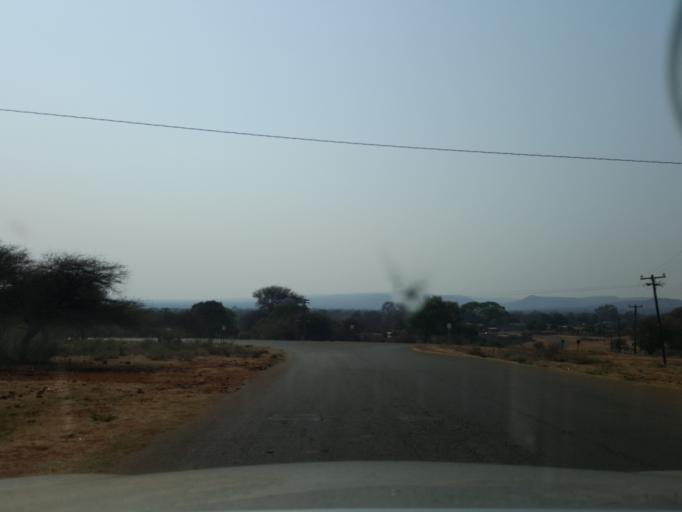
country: BW
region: South East
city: Lobatse
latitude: -25.2860
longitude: 25.8969
